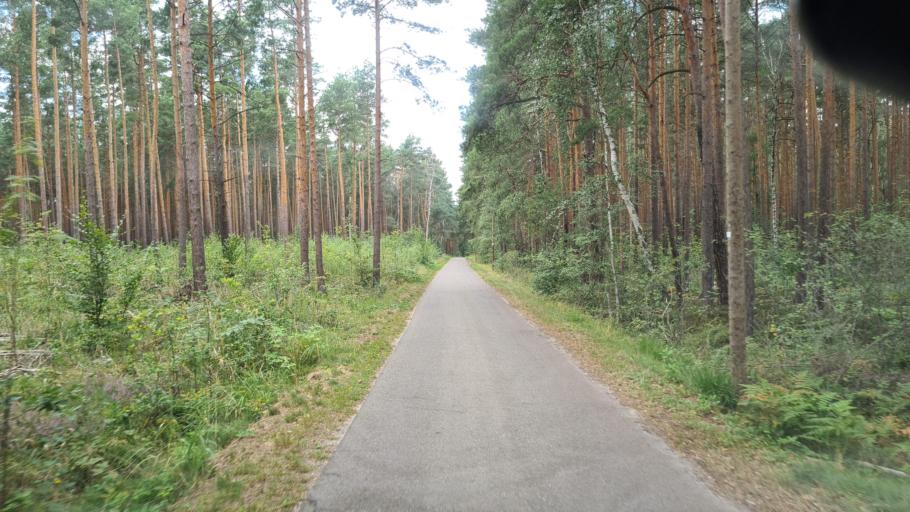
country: DE
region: Brandenburg
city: Sallgast
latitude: 51.5898
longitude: 13.8956
